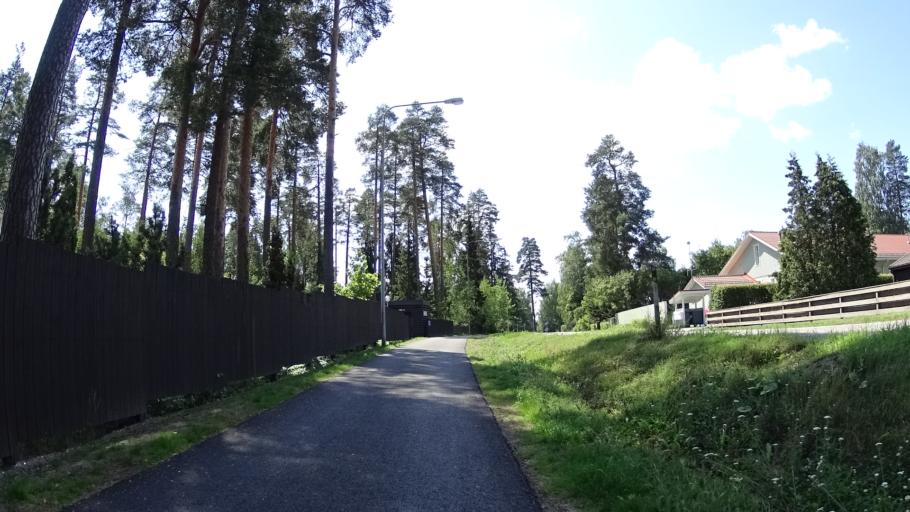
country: FI
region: Uusimaa
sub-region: Helsinki
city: Tuusula
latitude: 60.4074
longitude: 25.0136
